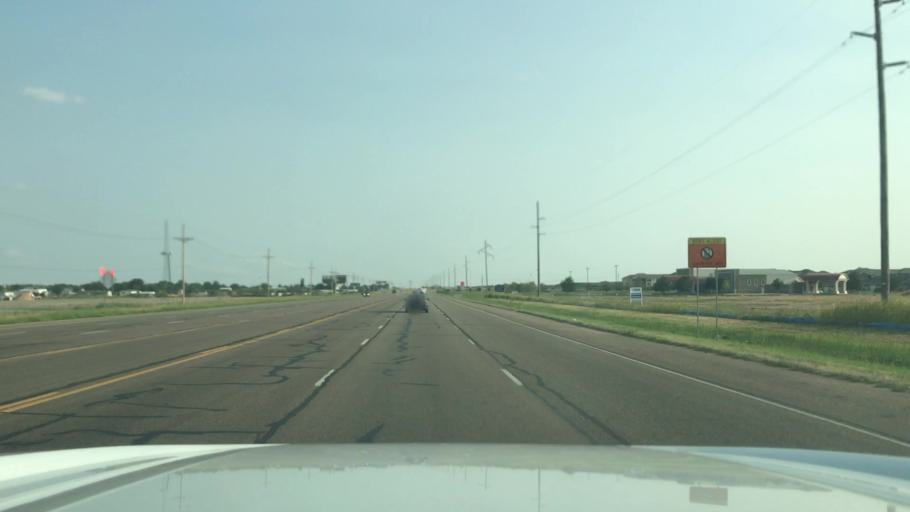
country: US
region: Texas
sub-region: Potter County
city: Amarillo
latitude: 35.1366
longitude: -101.9382
